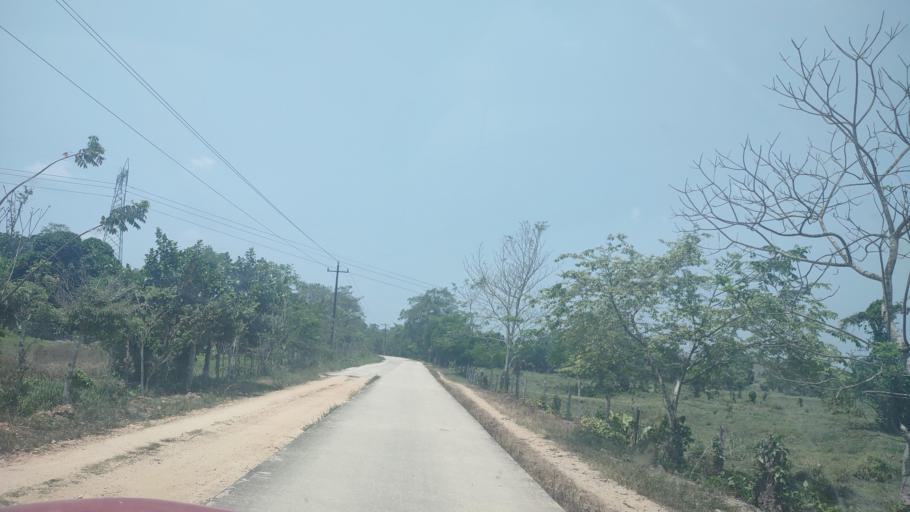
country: MX
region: Tabasco
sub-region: Huimanguillo
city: Francisco Rueda
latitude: 17.6922
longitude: -94.0463
